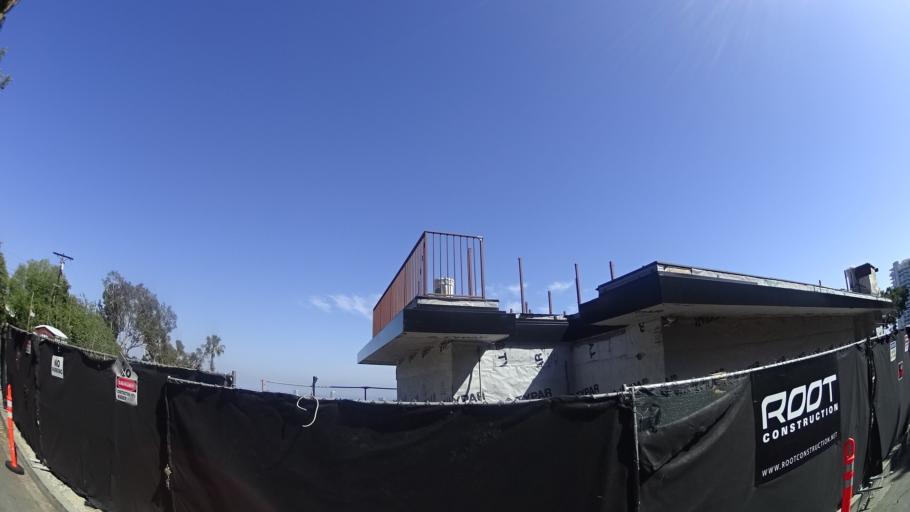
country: US
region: California
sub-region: Los Angeles County
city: Beverly Hills
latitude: 34.0939
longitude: -118.3906
